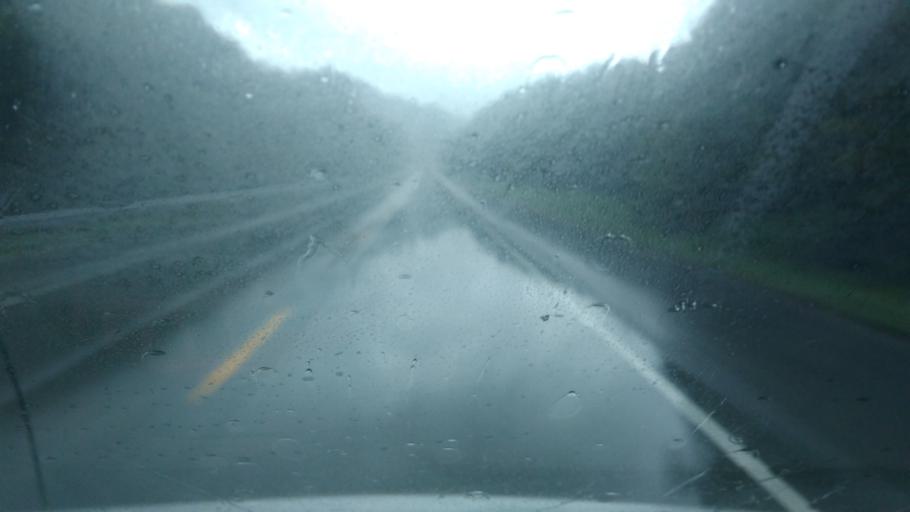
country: US
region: Kentucky
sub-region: Lewis County
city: Vanceburg
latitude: 38.5911
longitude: -83.2302
